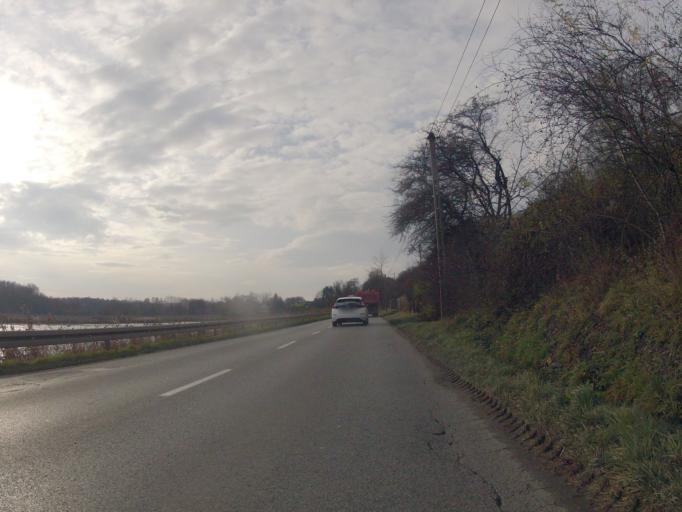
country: PL
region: Lesser Poland Voivodeship
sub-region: Powiat krakowski
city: Rzaska
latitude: 50.0902
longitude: 19.8221
